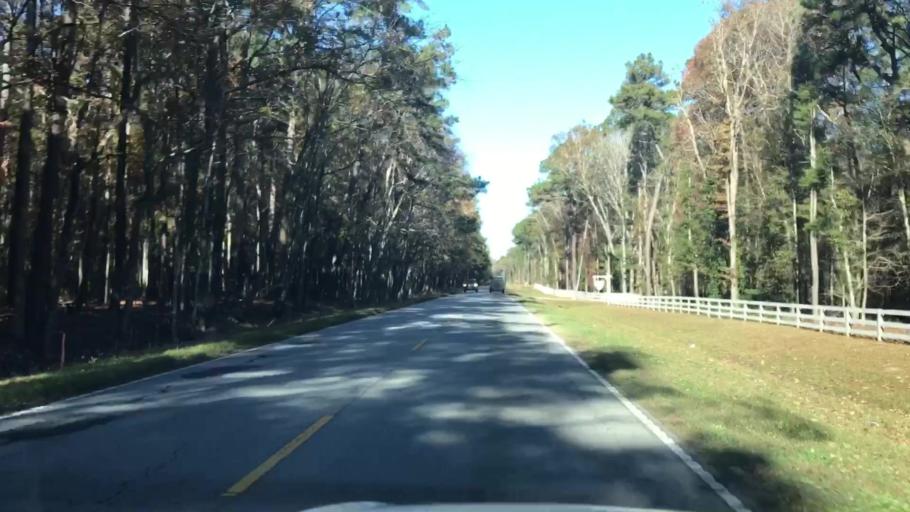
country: US
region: South Carolina
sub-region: Dorchester County
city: Centerville
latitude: 32.9268
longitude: -80.1678
